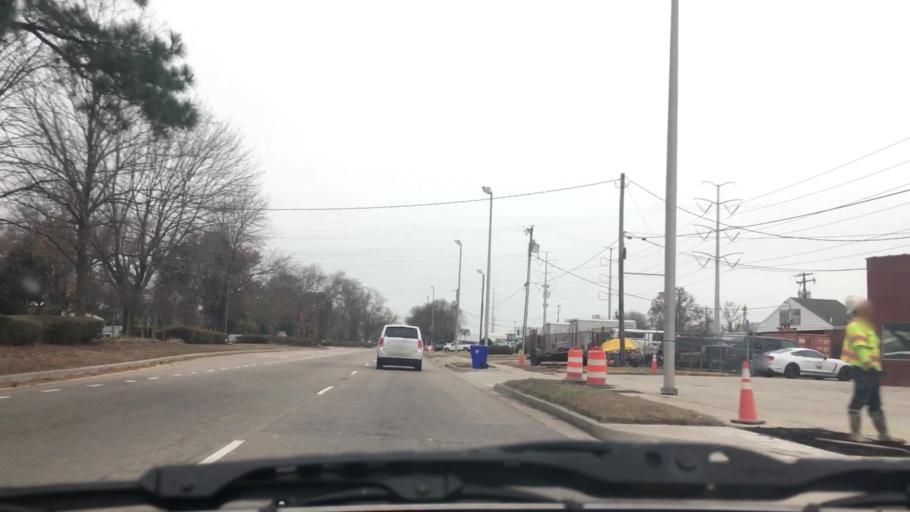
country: US
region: Virginia
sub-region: City of Norfolk
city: Norfolk
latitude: 36.8687
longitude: -76.2501
